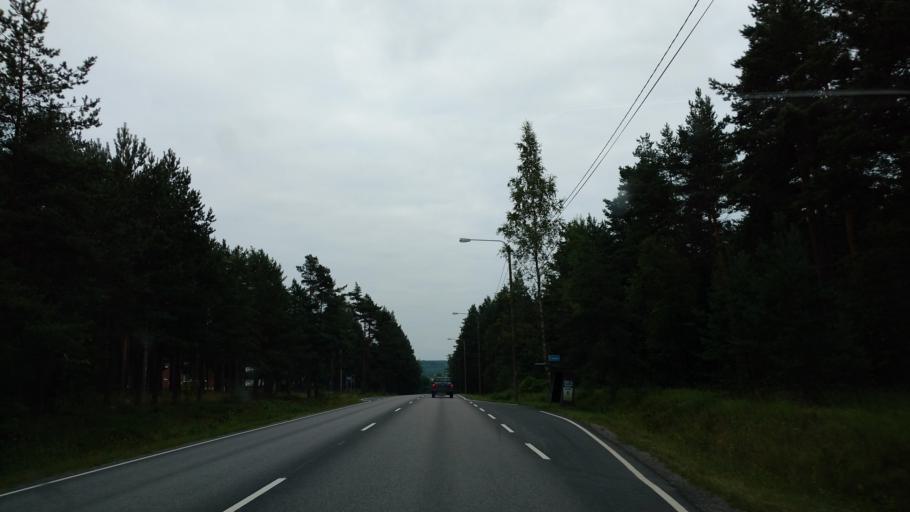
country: FI
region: Varsinais-Suomi
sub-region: Salo
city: Halikko
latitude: 60.4399
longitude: 23.0407
